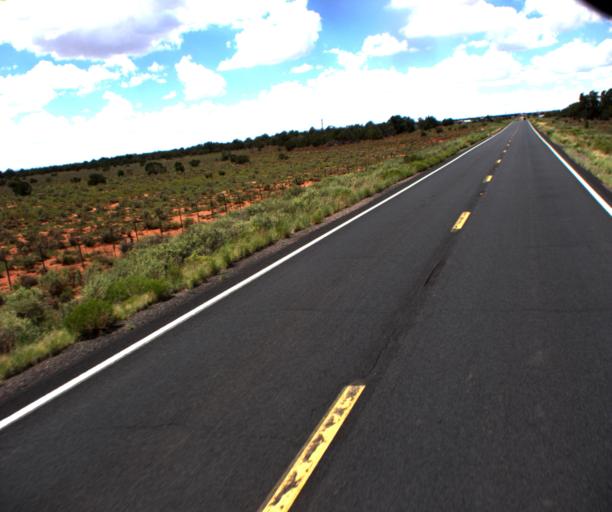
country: US
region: Arizona
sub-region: Coconino County
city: Williams
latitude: 35.6399
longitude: -112.1263
